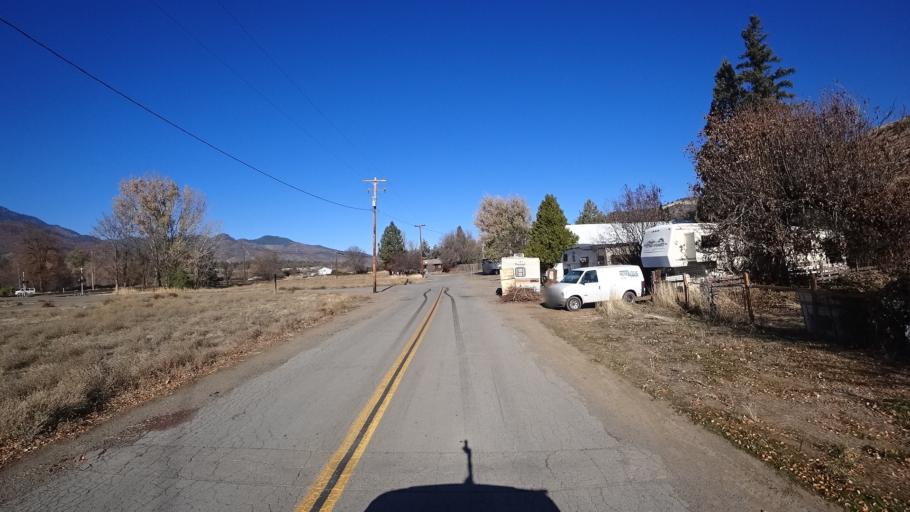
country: US
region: California
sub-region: Siskiyou County
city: Montague
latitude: 41.9105
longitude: -122.5545
